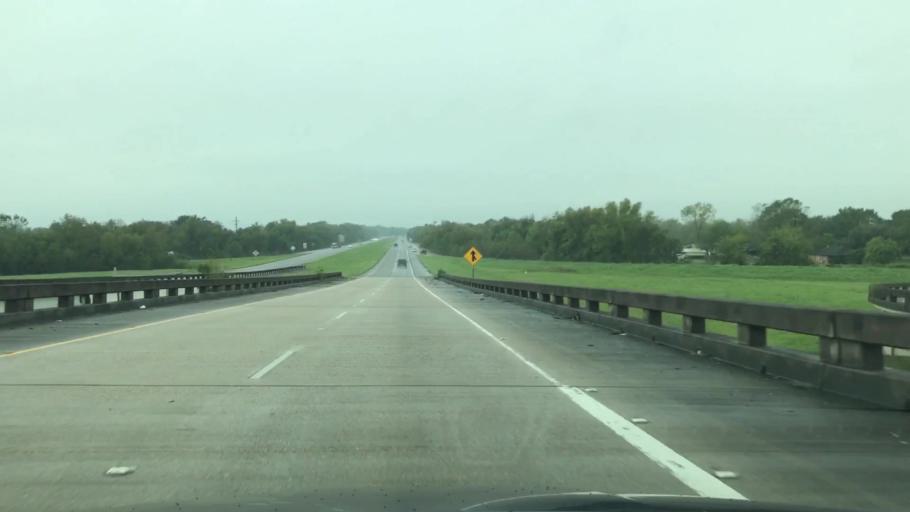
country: US
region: Louisiana
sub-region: Lafourche Parish
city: Raceland
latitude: 29.7063
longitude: -90.5737
